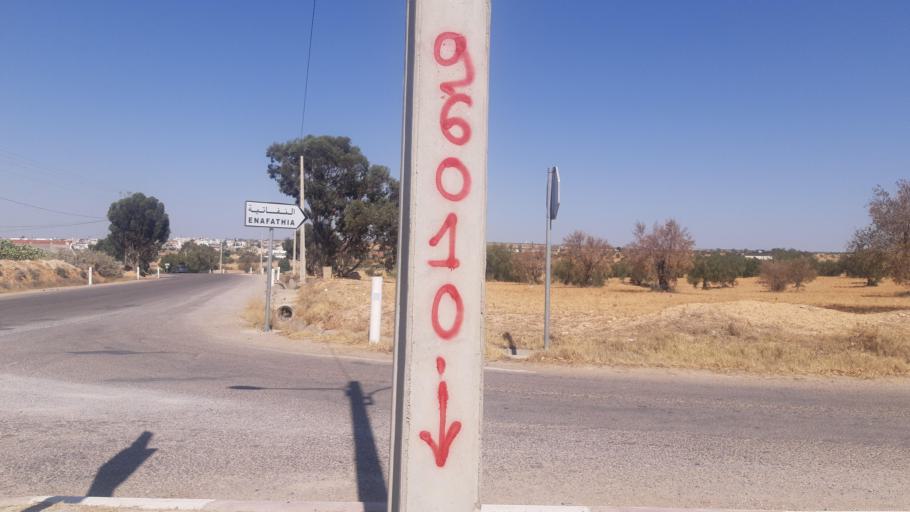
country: TN
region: Al Mahdiyah
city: Shurban
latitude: 35.2810
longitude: 10.3704
